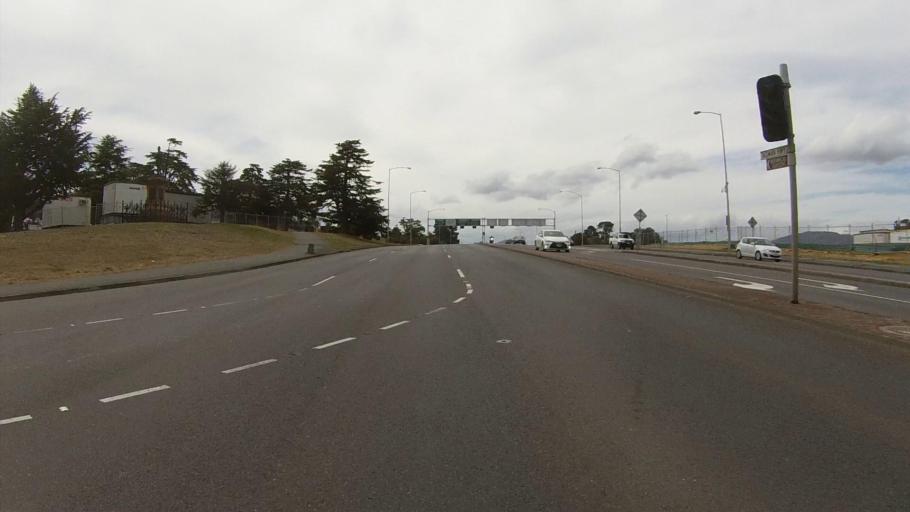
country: AU
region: Tasmania
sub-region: Hobart
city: Hobart
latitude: -42.8768
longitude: 147.3338
